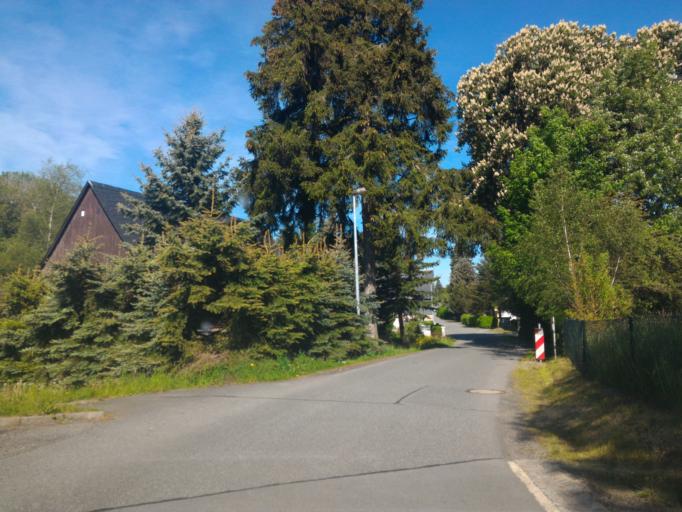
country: DE
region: Saxony
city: Leutersdorf
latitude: 50.9688
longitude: 14.6472
